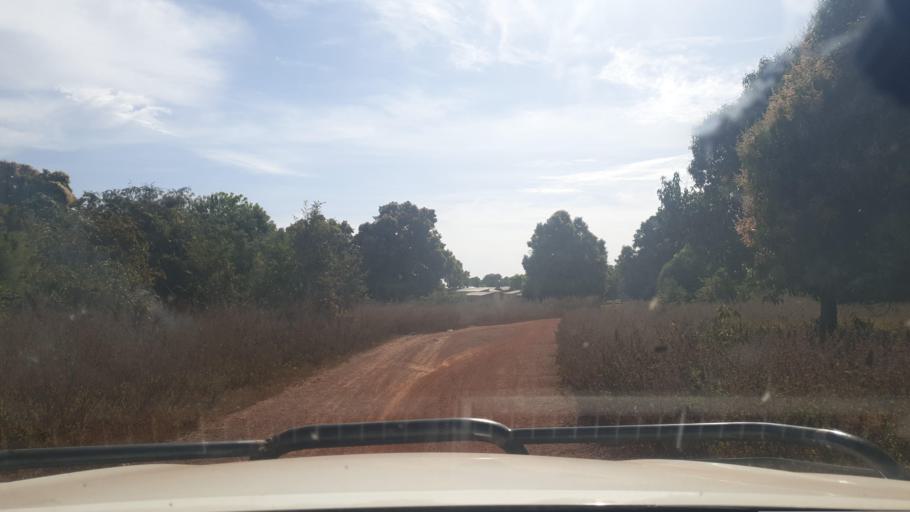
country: GN
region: Kankan
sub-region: Mandiana Prefecture
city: Mandiana
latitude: 10.4918
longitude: -8.1005
